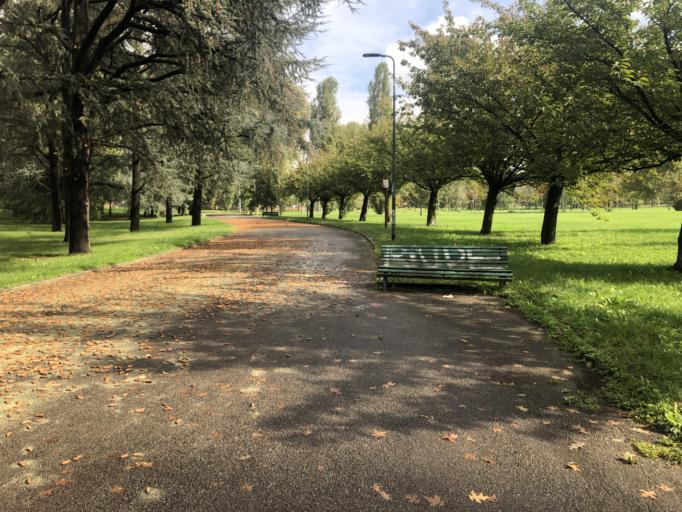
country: IT
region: Lombardy
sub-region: Citta metropolitana di Milano
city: Linate
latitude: 45.4644
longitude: 9.2598
